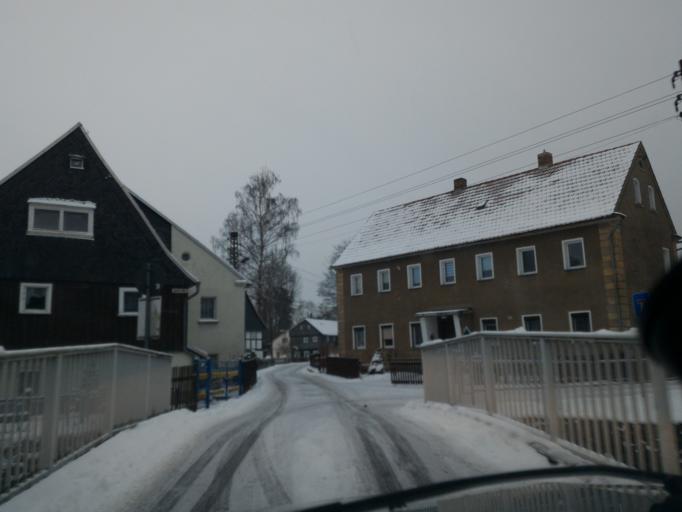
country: DE
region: Saxony
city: Seifhennersdorf
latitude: 50.9396
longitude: 14.5853
